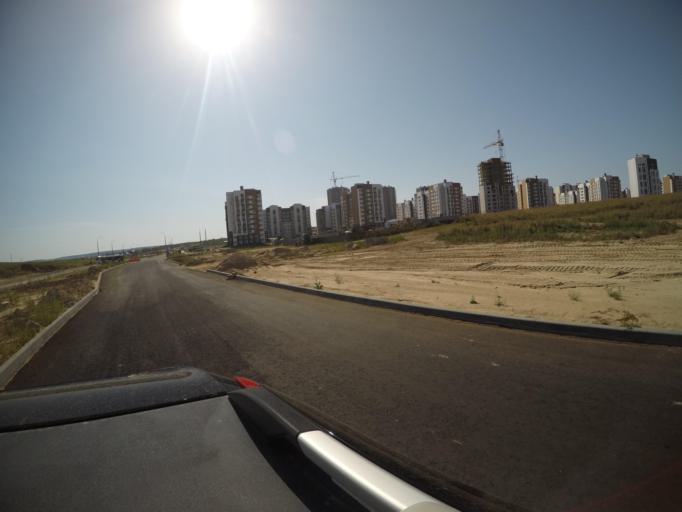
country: BY
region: Grodnenskaya
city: Hrodna
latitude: 53.7242
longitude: 23.8830
